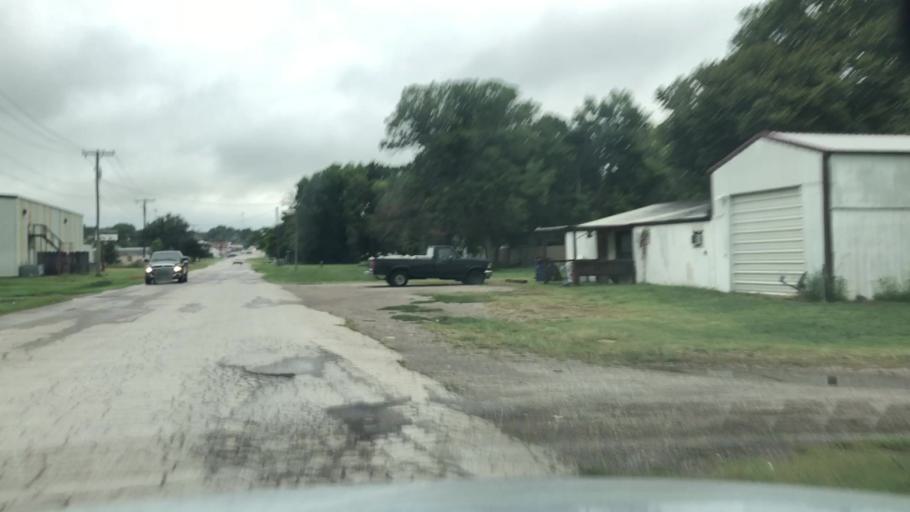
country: US
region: Oklahoma
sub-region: Nowata County
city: Nowata
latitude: 36.7013
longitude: -95.6303
